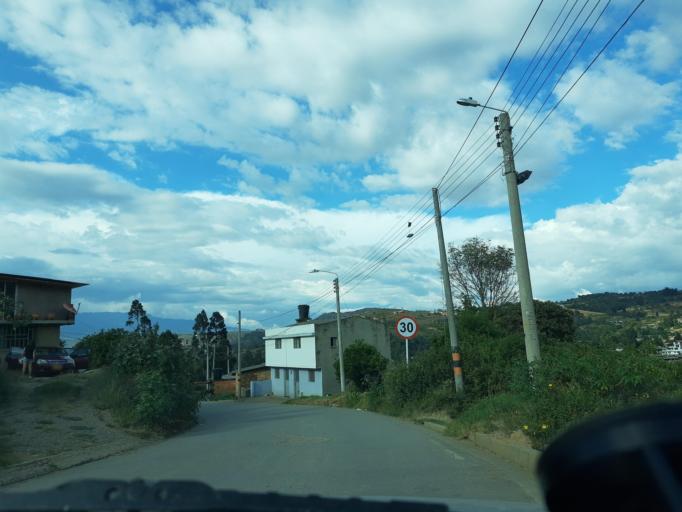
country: CO
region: Boyaca
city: Raquira
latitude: 5.5370
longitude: -73.6357
